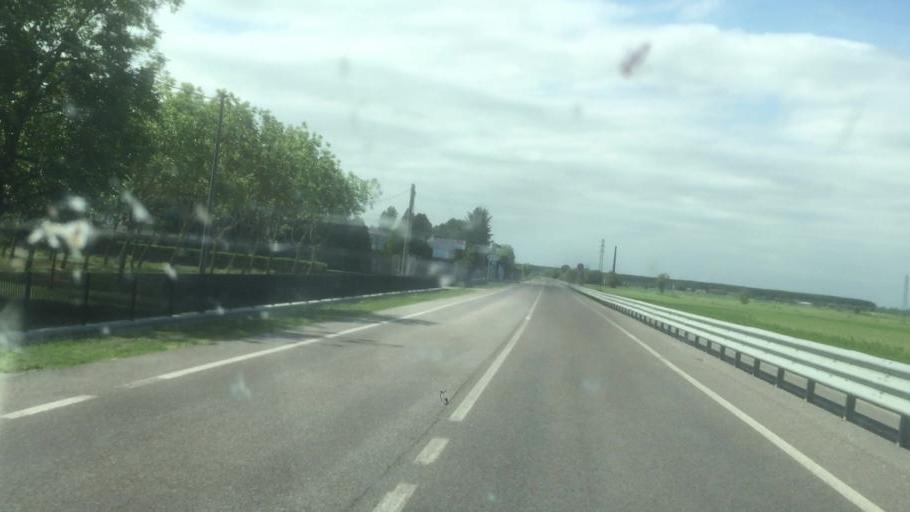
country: IT
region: Veneto
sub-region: Provincia di Rovigo
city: Ceneselli
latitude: 45.0070
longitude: 11.3682
